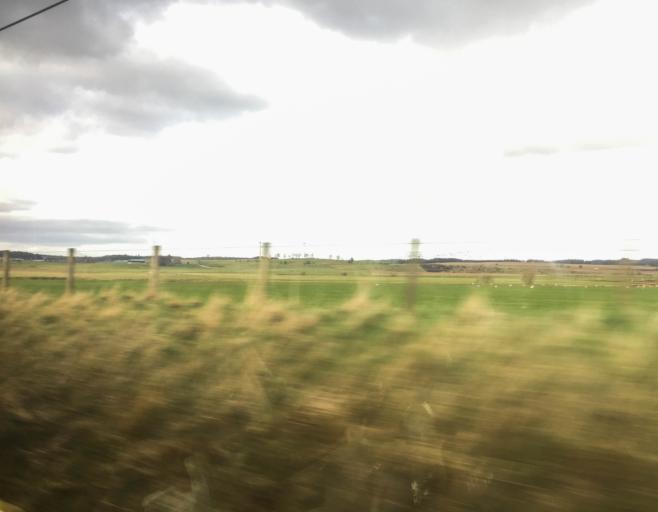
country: GB
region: Scotland
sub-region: South Lanarkshire
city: Carnwath
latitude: 55.6775
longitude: -3.6485
